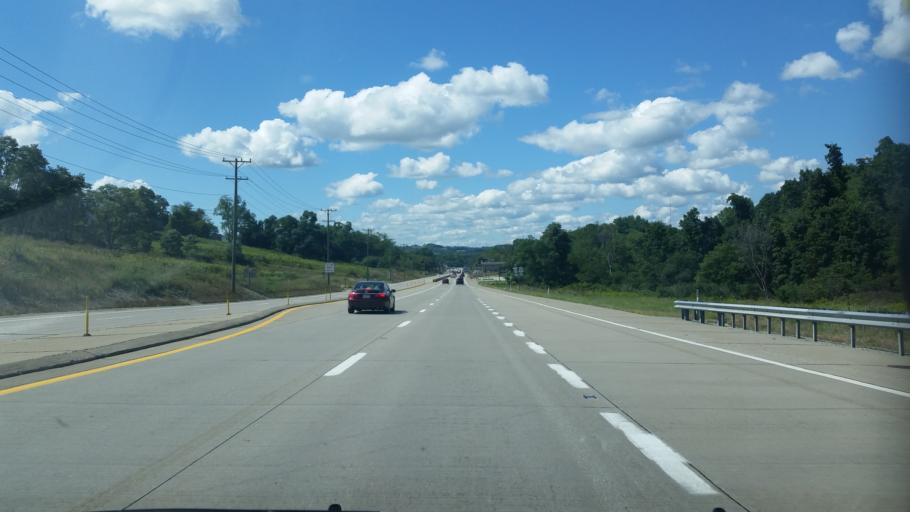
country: US
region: Pennsylvania
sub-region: Westmoreland County
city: Latrobe
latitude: 40.4020
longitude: -79.4125
